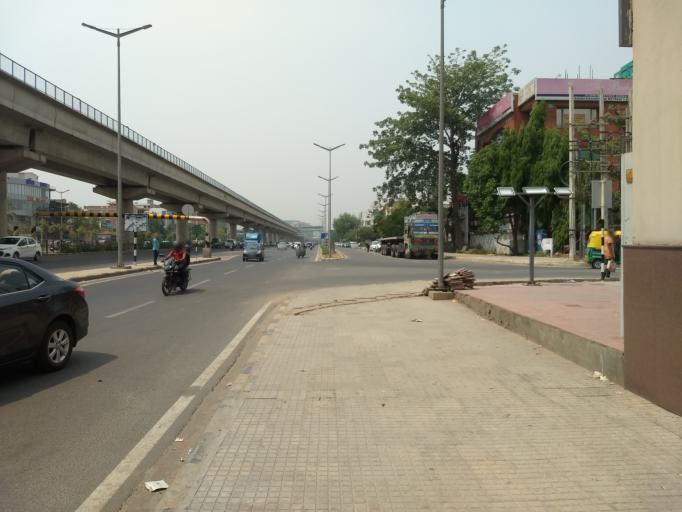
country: IN
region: Haryana
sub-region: Gurgaon
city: Gurgaon
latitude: 28.4719
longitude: 77.0943
